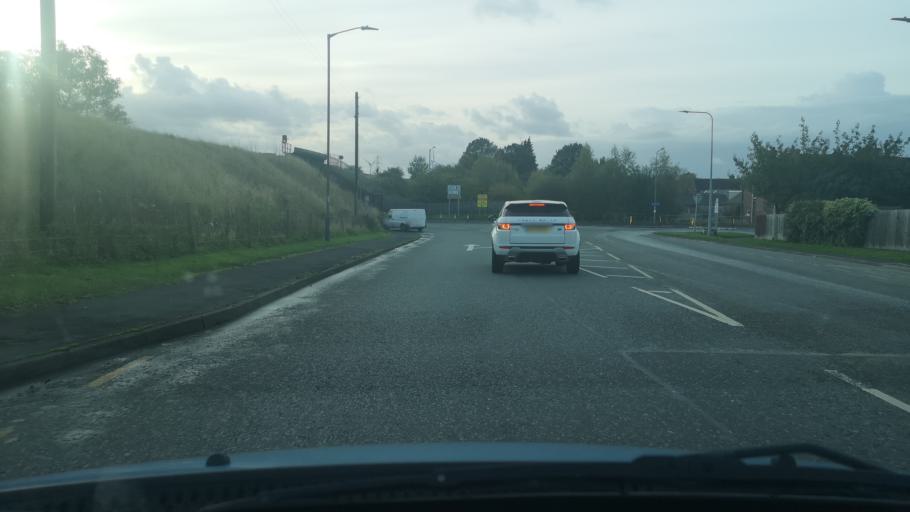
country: GB
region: England
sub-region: North Lincolnshire
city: Gunness
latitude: 53.5856
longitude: -0.7355
